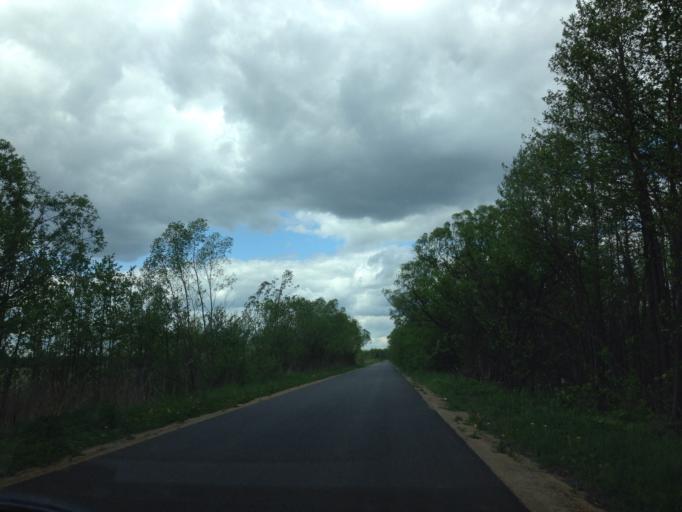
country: PL
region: Podlasie
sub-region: Powiat bialostocki
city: Tykocin
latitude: 53.2931
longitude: 22.6078
